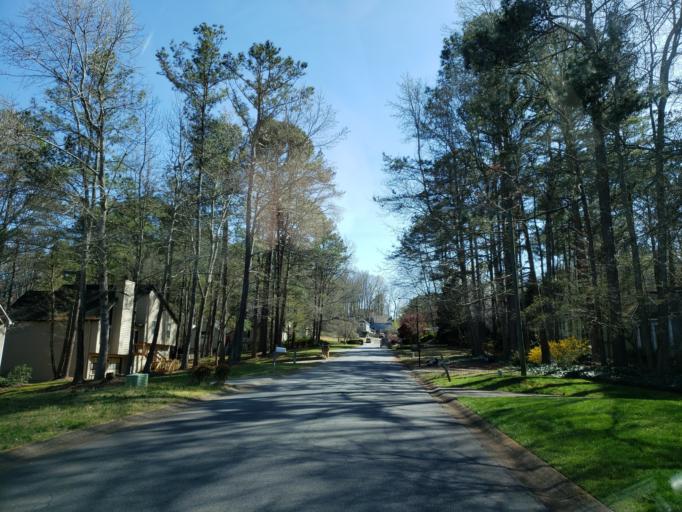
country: US
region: Georgia
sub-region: Cherokee County
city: Woodstock
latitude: 34.0380
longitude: -84.4904
